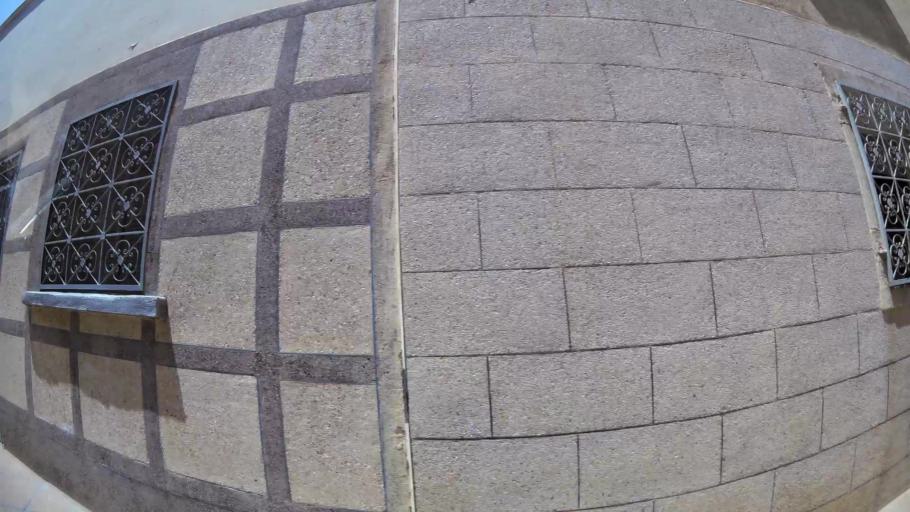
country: MA
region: Oriental
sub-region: Oujda-Angad
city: Oujda
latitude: 34.7000
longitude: -1.8968
